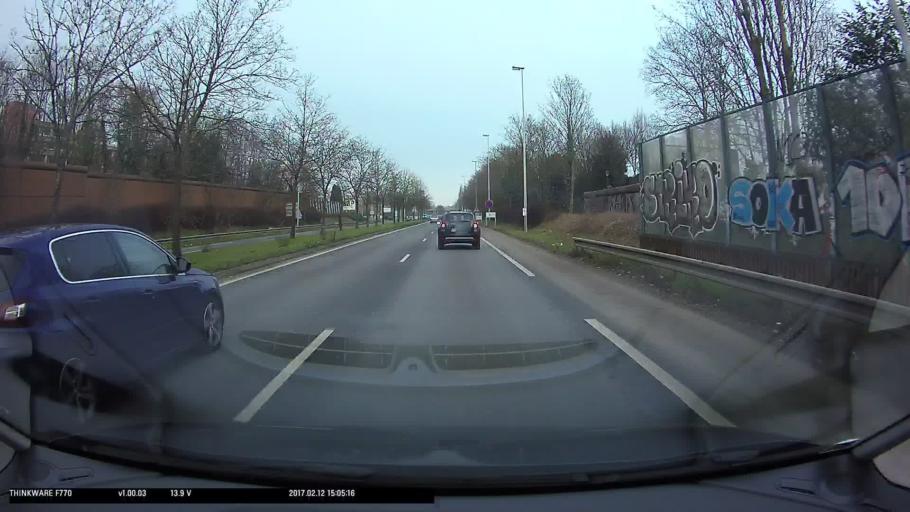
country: FR
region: Ile-de-France
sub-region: Departement du Val-d'Oise
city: Eragny
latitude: 49.0167
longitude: 2.0936
